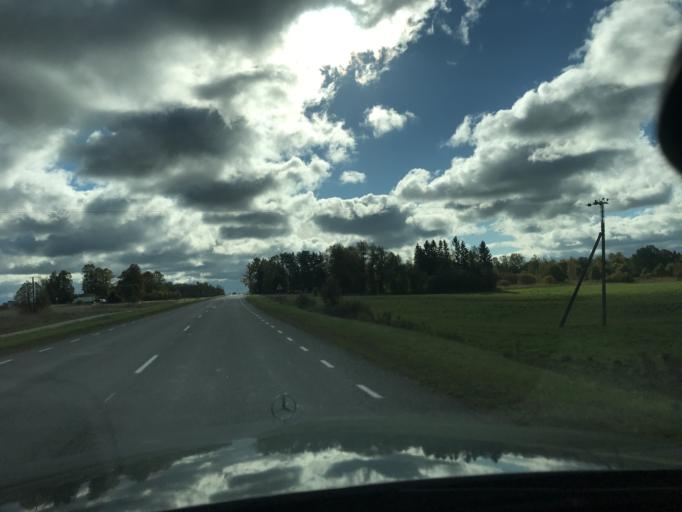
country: EE
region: Vorumaa
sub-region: Antsla vald
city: Vana-Antsla
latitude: 57.9390
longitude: 26.3098
